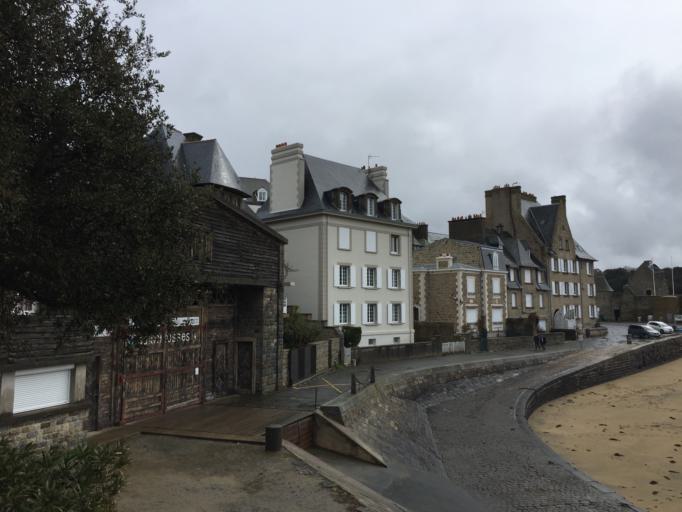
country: FR
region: Brittany
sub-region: Departement d'Ille-et-Vilaine
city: Saint-Malo
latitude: 48.6350
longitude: -2.0266
